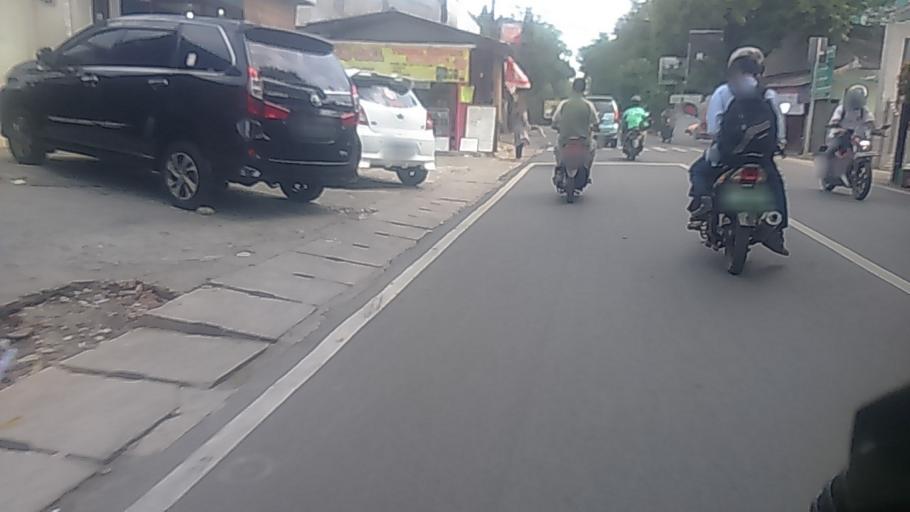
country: ID
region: West Java
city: Depok
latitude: -6.3378
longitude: 106.8055
